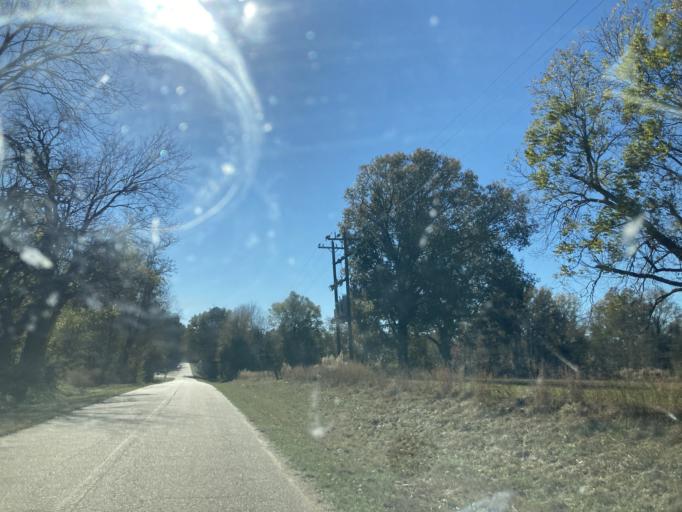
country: US
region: Mississippi
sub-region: Hinds County
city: Lynchburg
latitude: 32.5840
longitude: -90.5697
